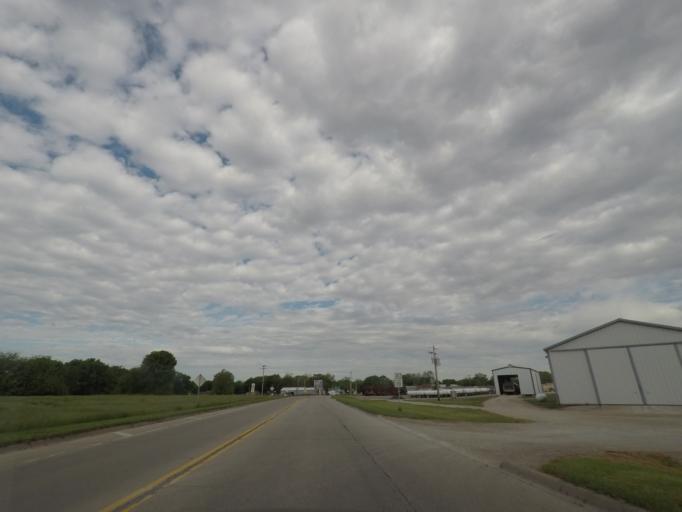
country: US
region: Illinois
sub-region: Logan County
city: Lincoln
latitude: 40.1474
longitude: -89.3500
